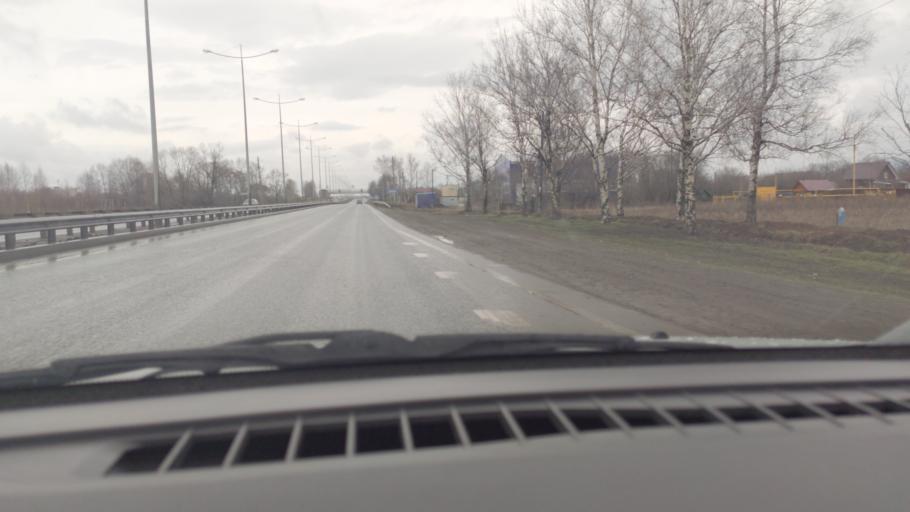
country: RU
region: Perm
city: Kultayevo
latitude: 57.9303
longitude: 56.0221
